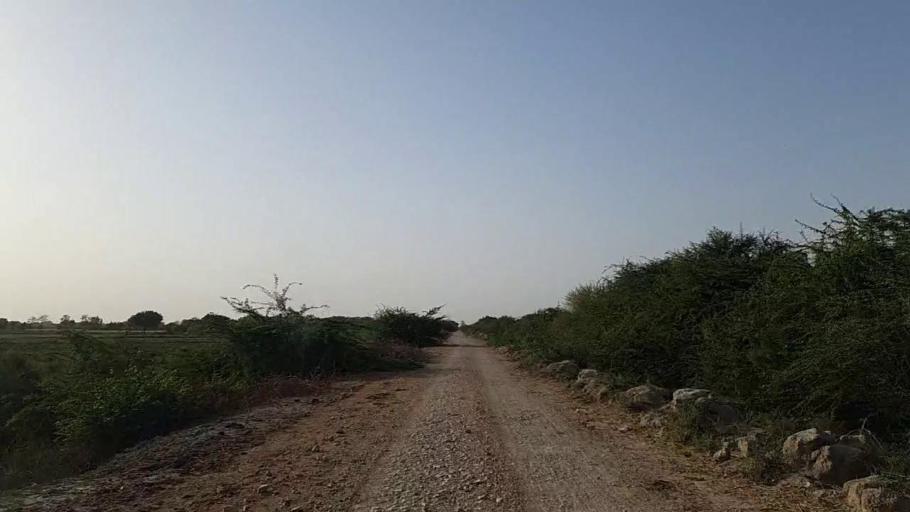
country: PK
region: Sindh
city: Jati
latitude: 24.3377
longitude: 68.1514
